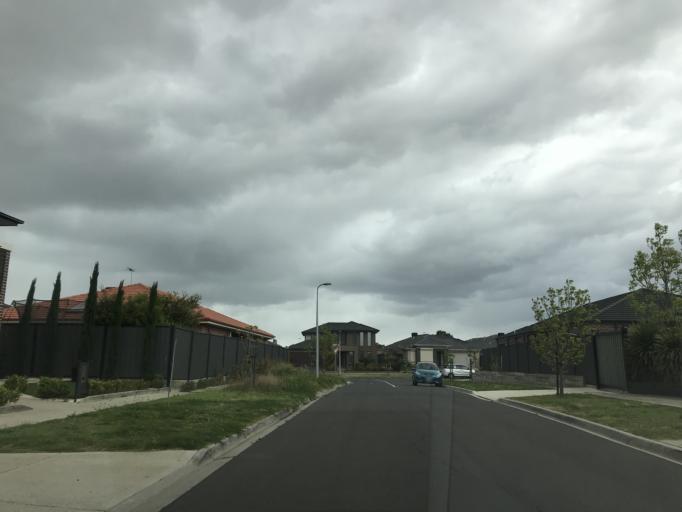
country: AU
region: Victoria
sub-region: Brimbank
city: Derrimut
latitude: -37.7855
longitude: 144.7625
